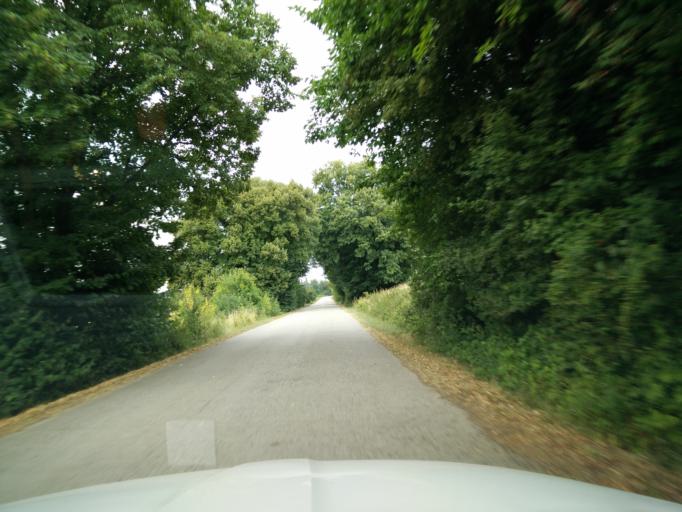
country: SK
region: Nitriansky
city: Novaky
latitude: 48.7341
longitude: 18.5460
